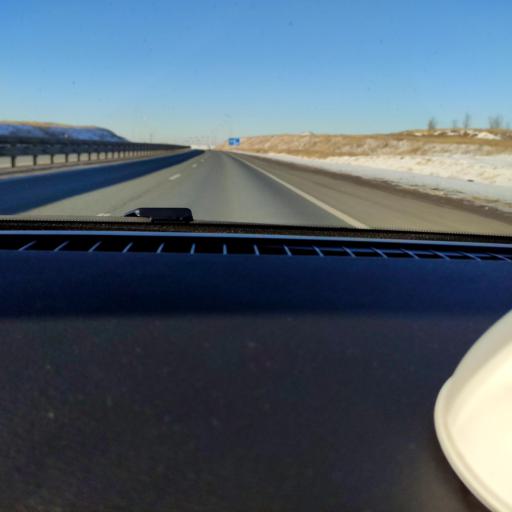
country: RU
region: Samara
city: Smyshlyayevka
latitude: 53.1466
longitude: 50.4063
